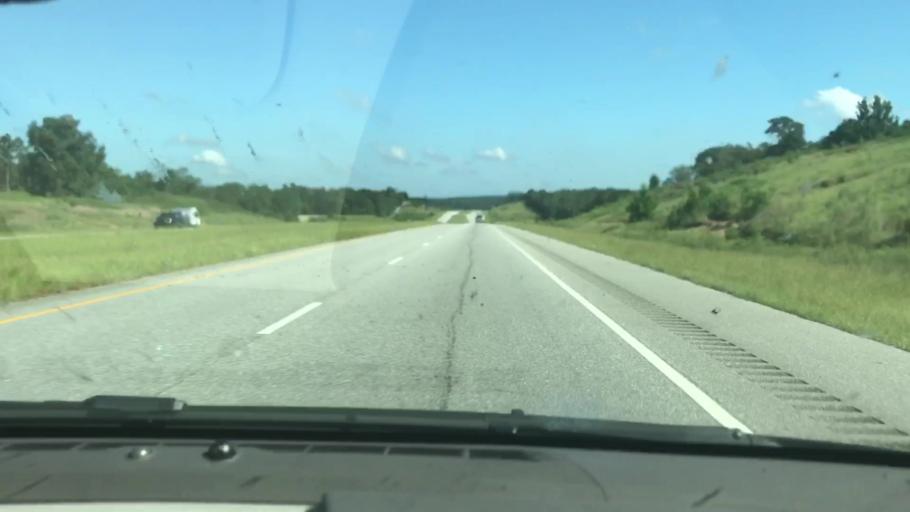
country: US
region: Alabama
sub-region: Barbour County
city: Eufaula
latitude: 32.0970
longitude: -85.1498
